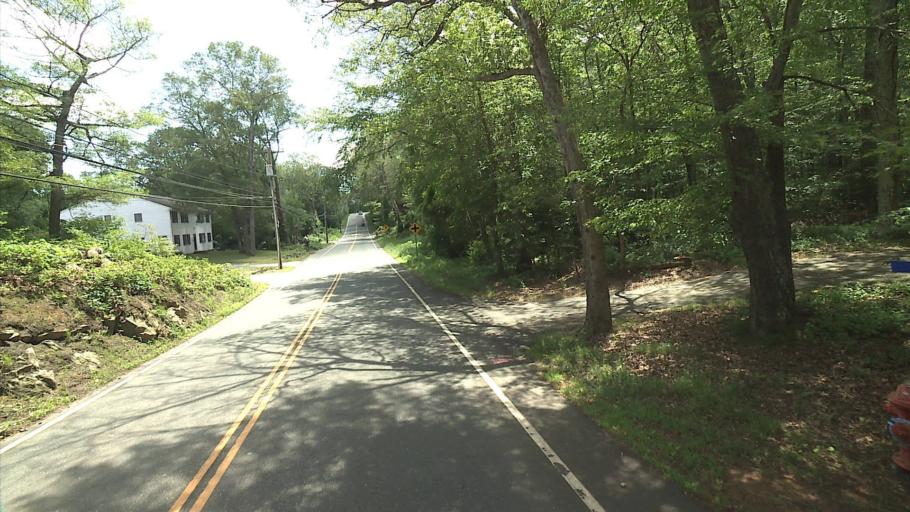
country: US
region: Connecticut
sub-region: New London County
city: Old Mystic
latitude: 41.3821
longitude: -71.9782
